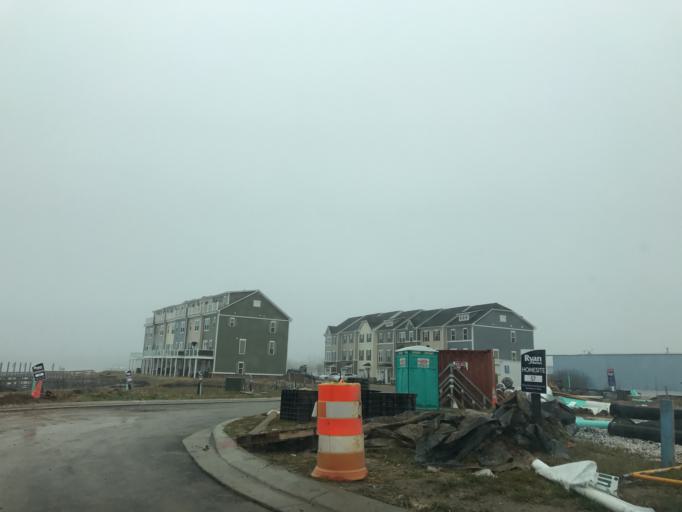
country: US
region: Maryland
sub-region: Baltimore County
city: Dundalk
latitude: 39.2561
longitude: -76.4962
